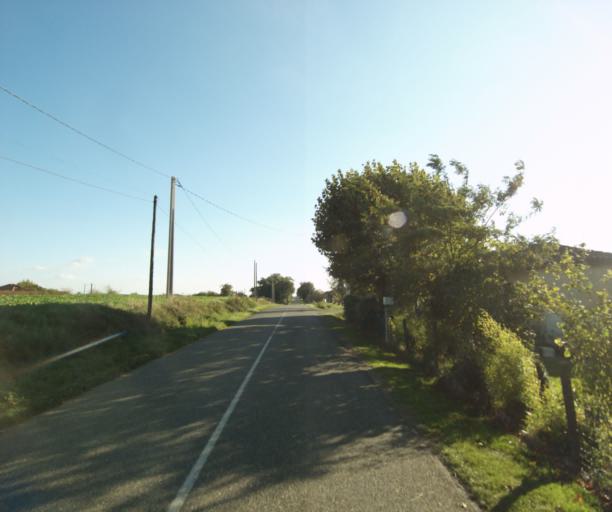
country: FR
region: Midi-Pyrenees
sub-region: Departement du Gers
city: Eauze
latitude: 43.7691
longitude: 0.1292
